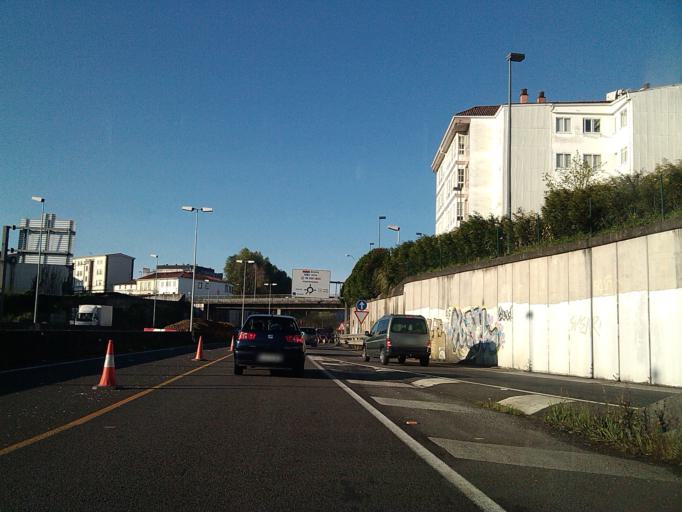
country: ES
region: Galicia
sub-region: Provincia da Coruna
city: Santiago de Compostela
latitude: 42.8669
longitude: -8.5530
